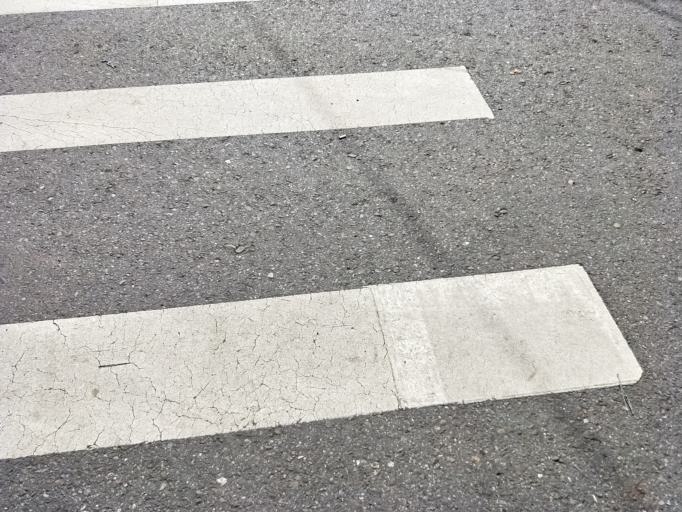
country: TW
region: Taiwan
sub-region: Yilan
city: Yilan
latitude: 24.7585
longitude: 121.7568
